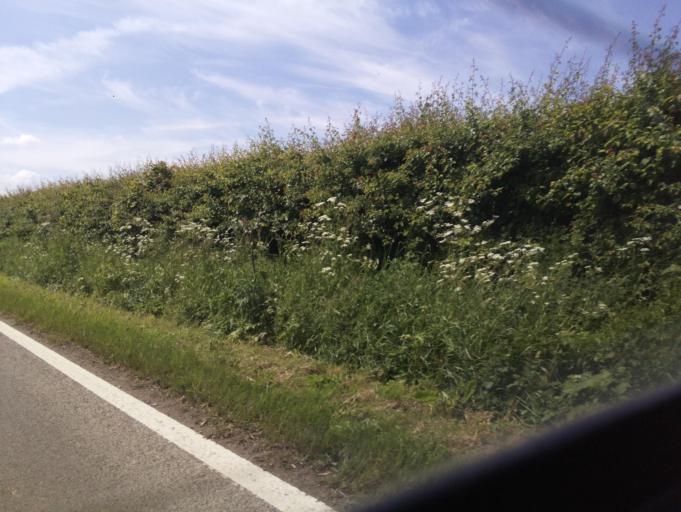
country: GB
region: England
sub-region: North Lincolnshire
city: Manton
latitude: 53.5063
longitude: -0.5827
